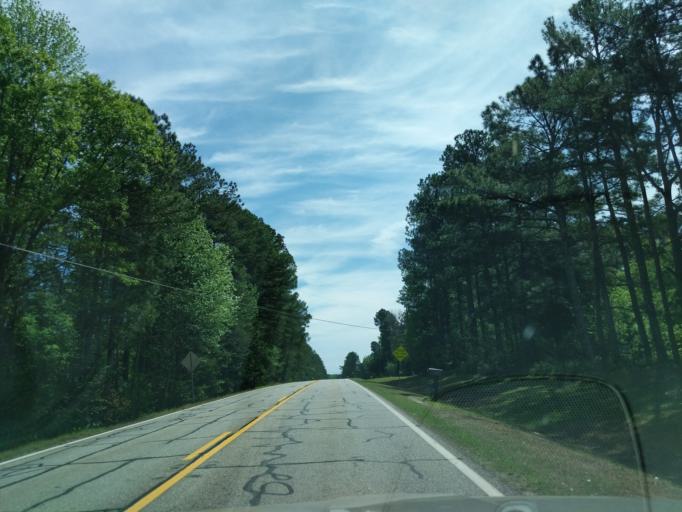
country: US
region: Georgia
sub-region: Columbia County
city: Appling
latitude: 33.6115
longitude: -82.3538
